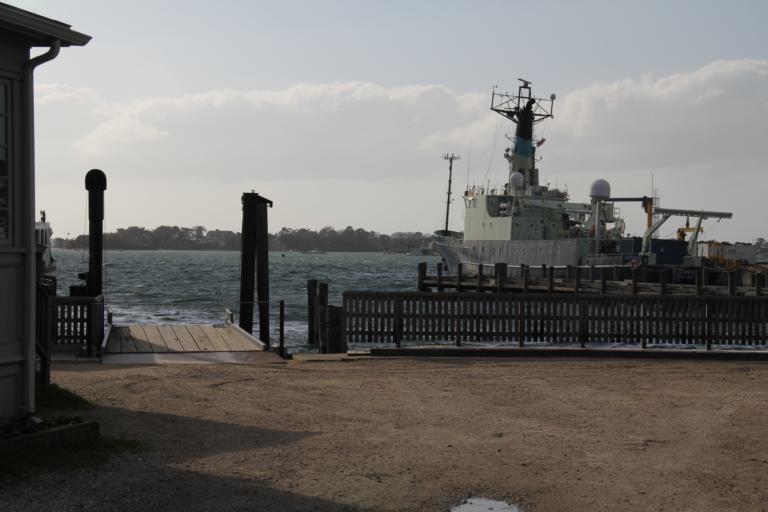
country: US
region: Massachusetts
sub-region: Barnstable County
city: Falmouth
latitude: 41.5234
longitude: -70.6700
